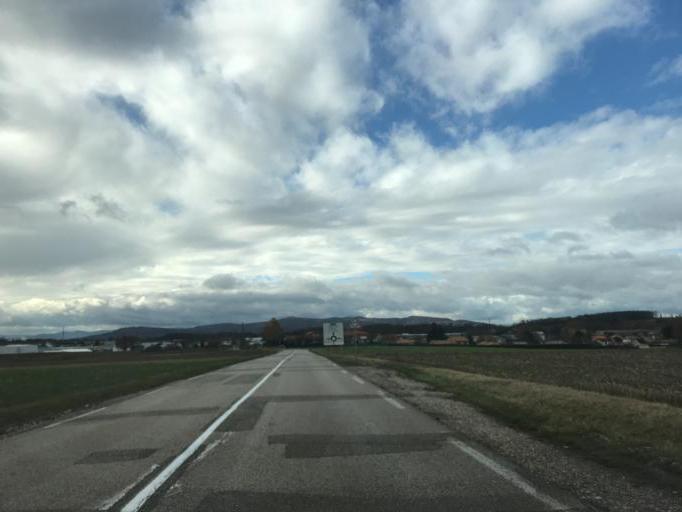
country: FR
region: Rhone-Alpes
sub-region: Departement de l'Ain
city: Mionnay
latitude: 45.8671
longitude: 4.9220
